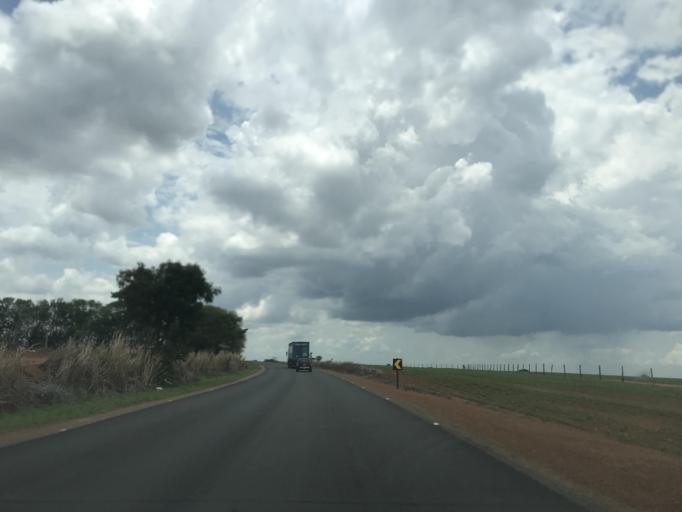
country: BR
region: Goias
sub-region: Vianopolis
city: Vianopolis
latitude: -16.7866
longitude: -48.5220
